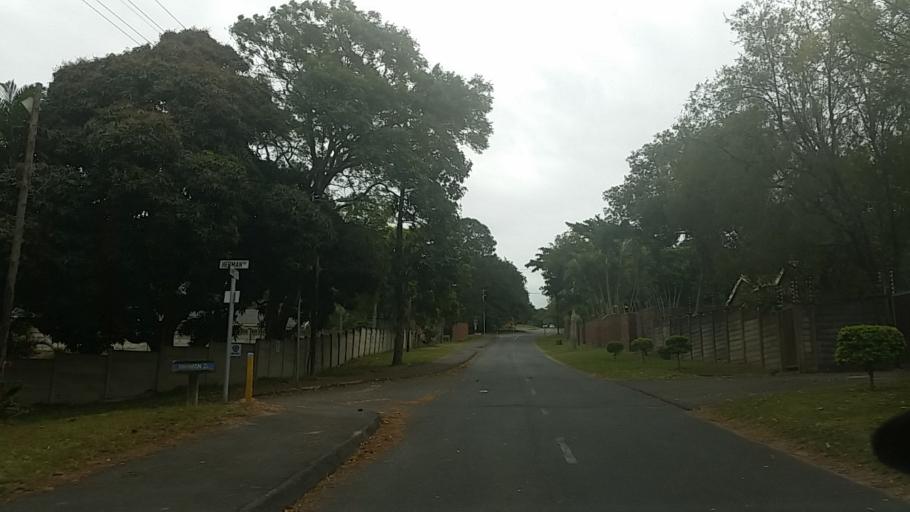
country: ZA
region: KwaZulu-Natal
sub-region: eThekwini Metropolitan Municipality
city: Berea
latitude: -29.8411
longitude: 30.9414
